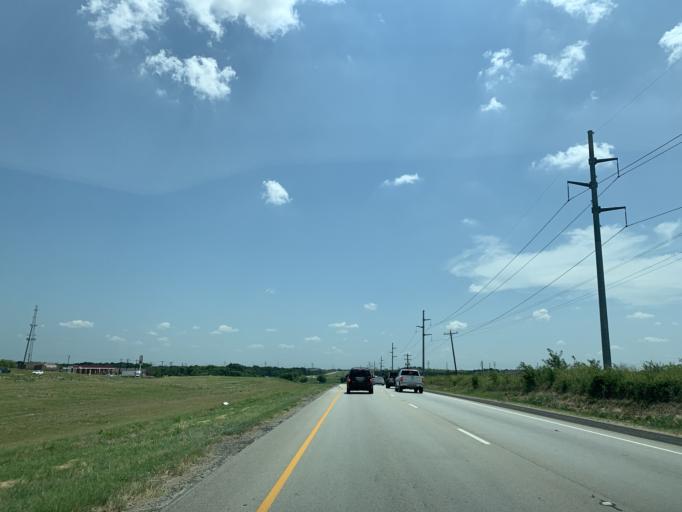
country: US
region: Texas
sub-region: Denton County
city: Roanoke
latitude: 33.0246
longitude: -97.2615
